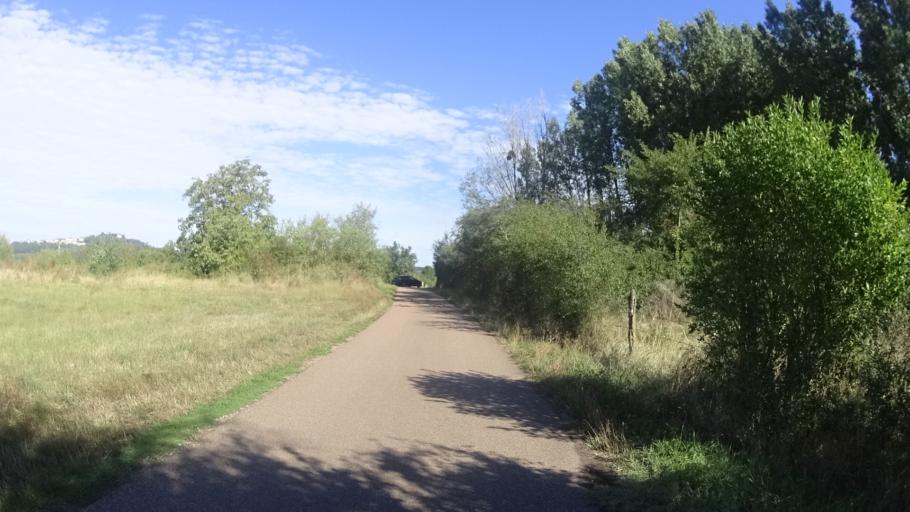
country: FR
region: Centre
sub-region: Departement du Cher
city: Sancerre
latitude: 47.3206
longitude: 2.8688
